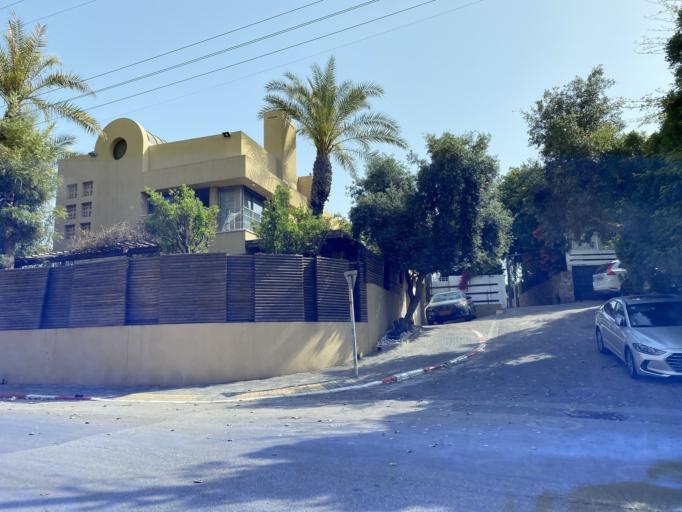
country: IL
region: Tel Aviv
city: Herzliya Pituah
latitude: 32.1744
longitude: 34.8061
